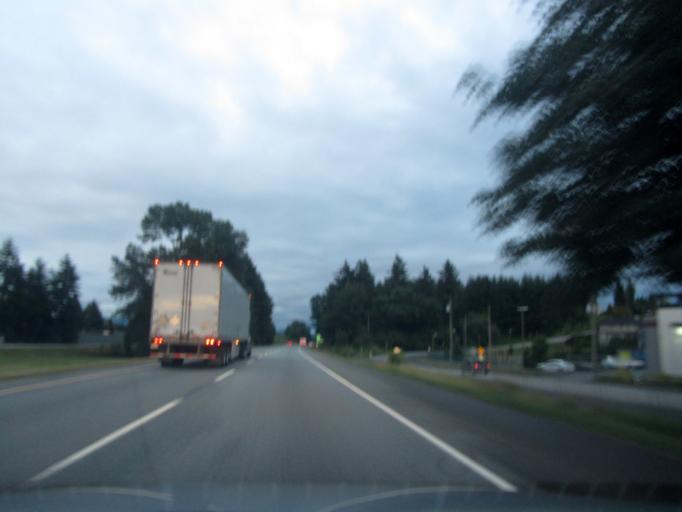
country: US
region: Washington
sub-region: Whatcom County
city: Sumas
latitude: 49.0452
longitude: -122.3526
